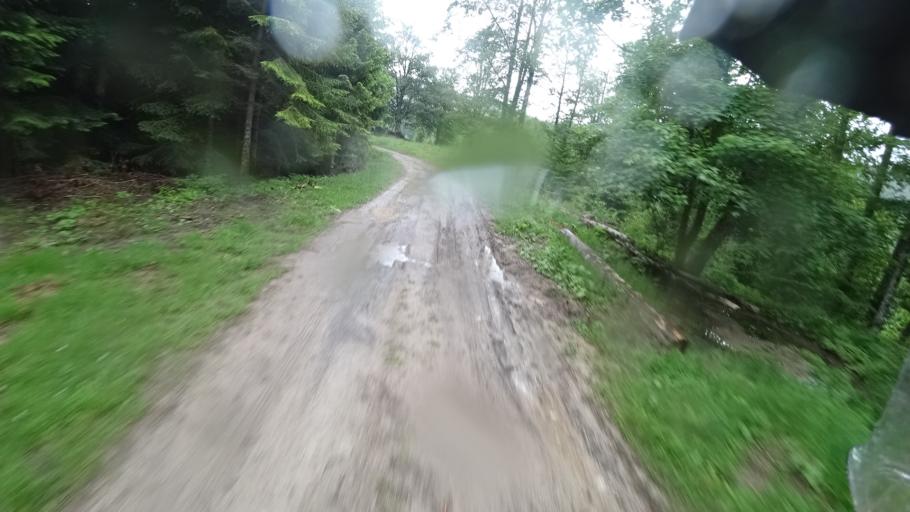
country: HR
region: Primorsko-Goranska
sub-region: Grad Delnice
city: Delnice
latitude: 45.3517
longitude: 14.9062
